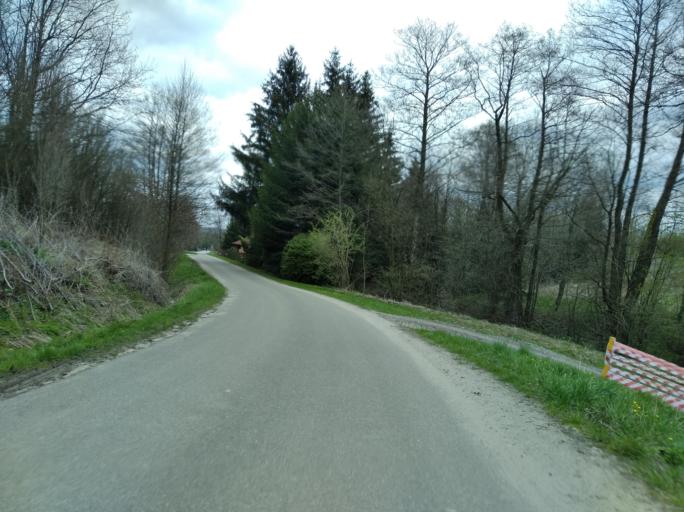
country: PL
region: Subcarpathian Voivodeship
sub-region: Powiat strzyzowski
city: Wysoka Strzyzowska
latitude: 49.8318
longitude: 21.7112
